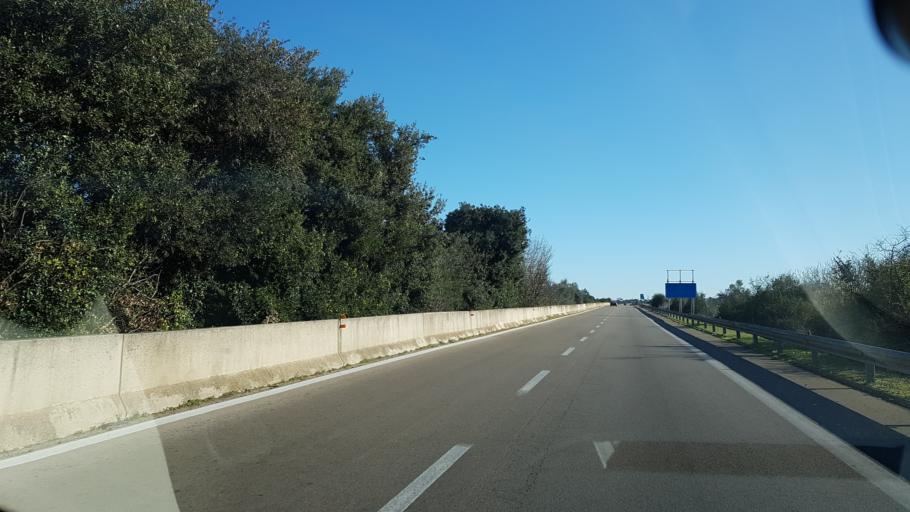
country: IT
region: Apulia
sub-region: Provincia di Lecce
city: Taviano
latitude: 40.0093
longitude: 18.0540
